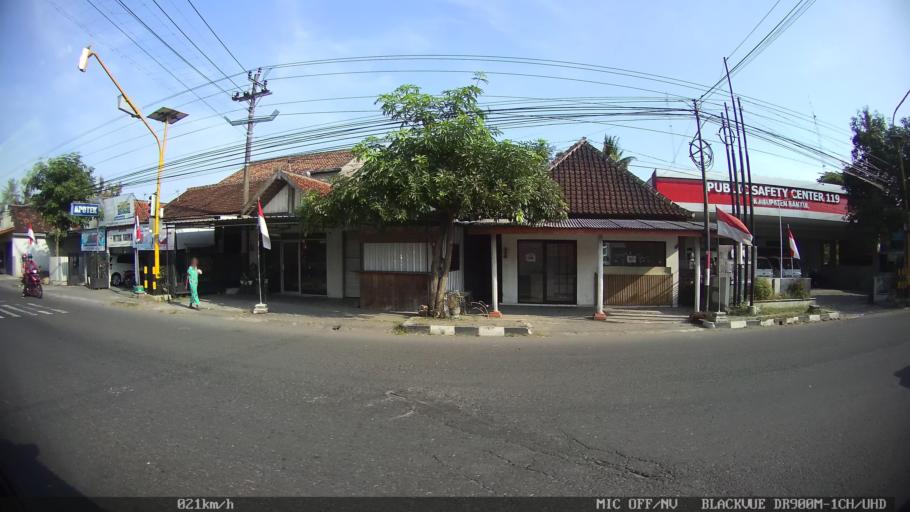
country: ID
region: Daerah Istimewa Yogyakarta
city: Pandak
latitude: -7.9059
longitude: 110.3150
